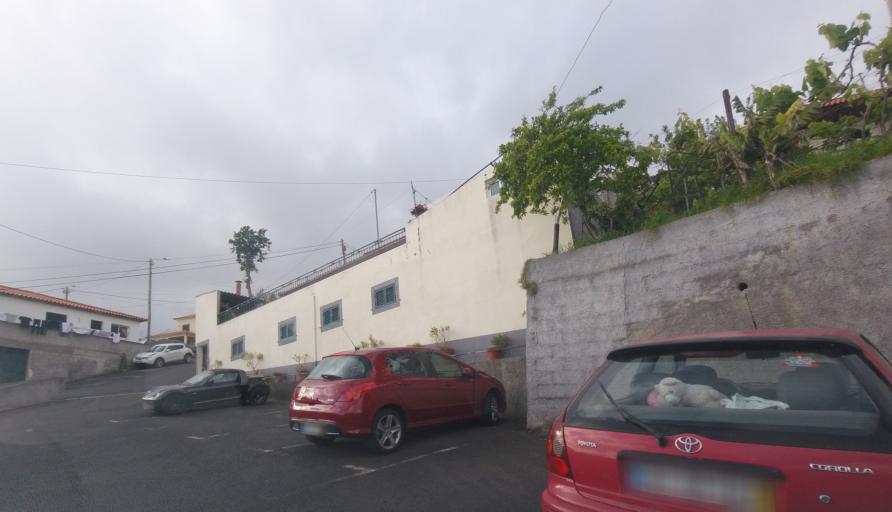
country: PT
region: Madeira
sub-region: Funchal
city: Nossa Senhora do Monte
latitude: 32.6794
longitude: -16.9102
